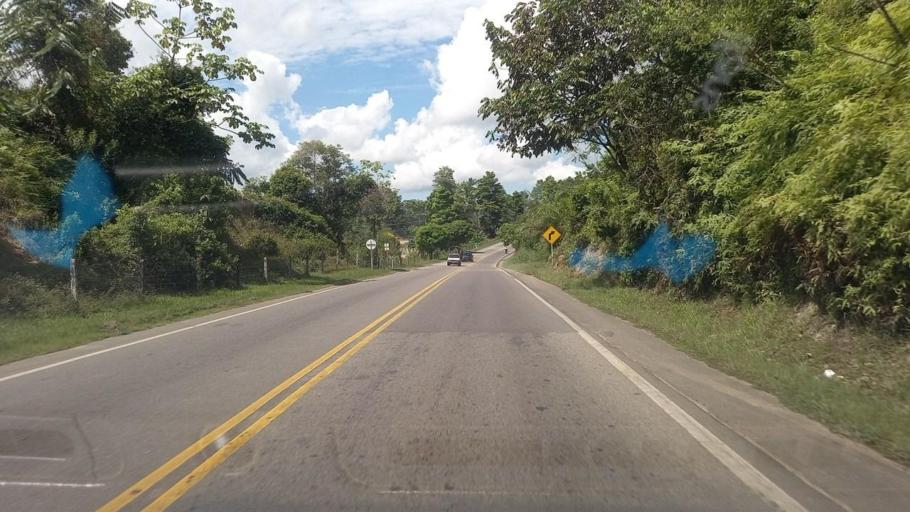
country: CO
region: Santander
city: Barrancabermeja
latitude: 7.1201
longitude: -73.5990
